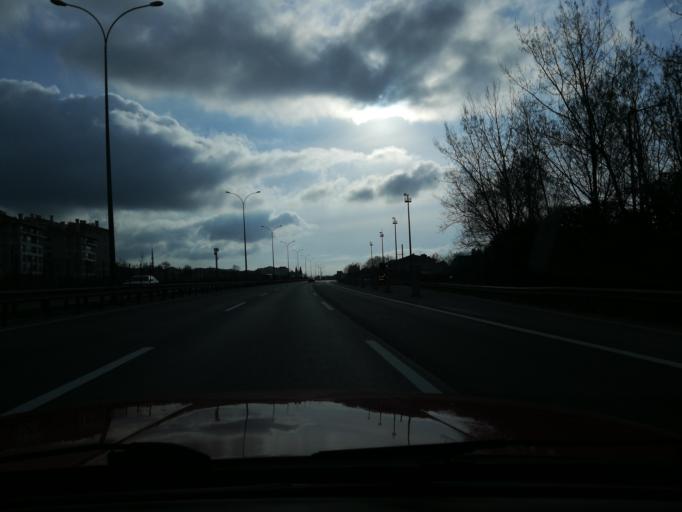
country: TR
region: Kocaeli
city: Derince
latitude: 40.7691
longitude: 29.8335
